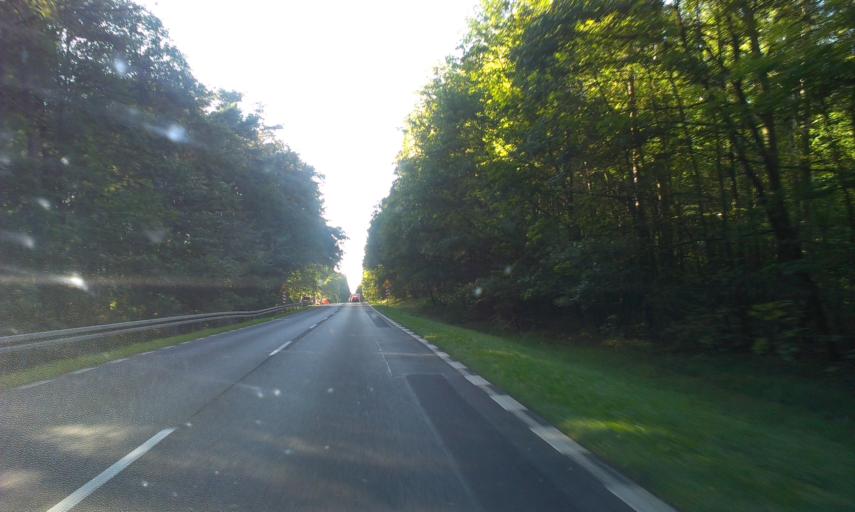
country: PL
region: Kujawsko-Pomorskie
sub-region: Powiat swiecki
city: Swiekatowo
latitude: 53.4864
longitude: 18.1197
